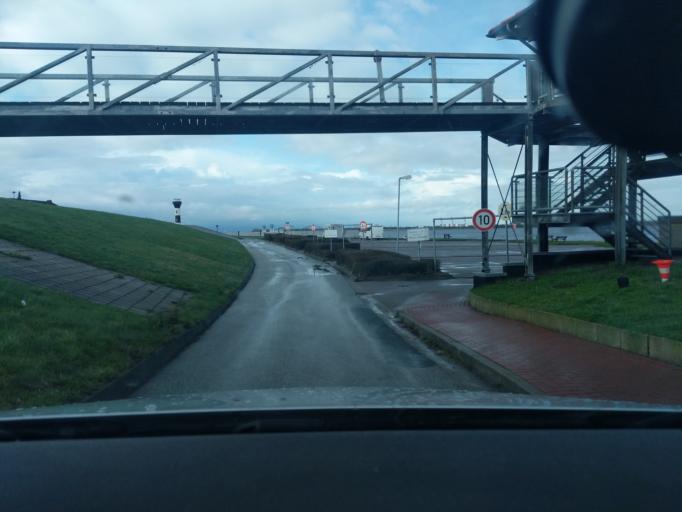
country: DE
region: Schleswig-Holstein
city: Haseldorf
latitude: 53.6034
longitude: 9.5596
